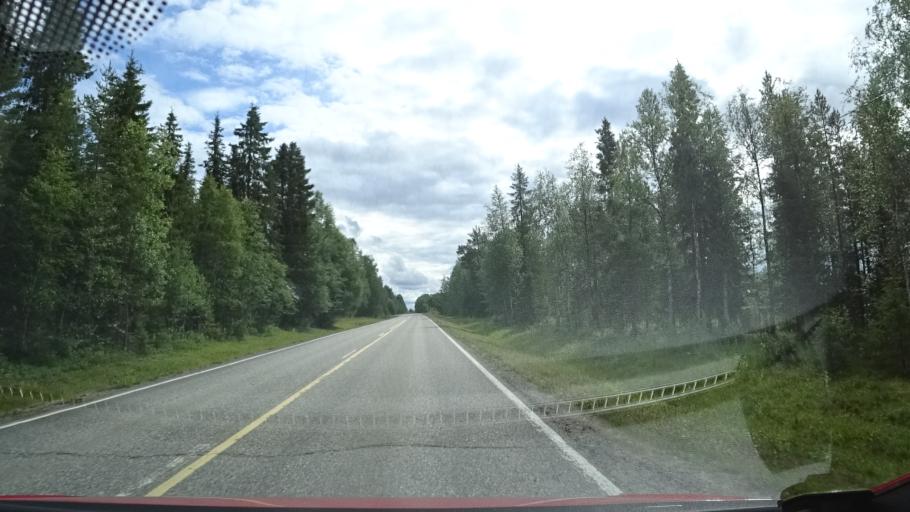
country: FI
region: Lapland
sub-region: Tunturi-Lappi
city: Kittilae
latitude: 67.4731
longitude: 24.9396
